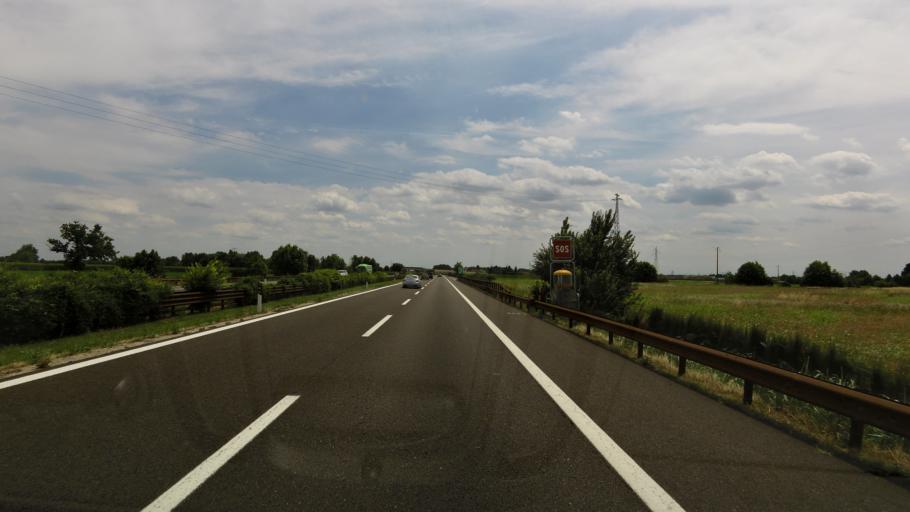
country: IT
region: Lombardy
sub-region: Provincia di Mantova
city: Mottella
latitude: 45.1890
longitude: 10.8485
